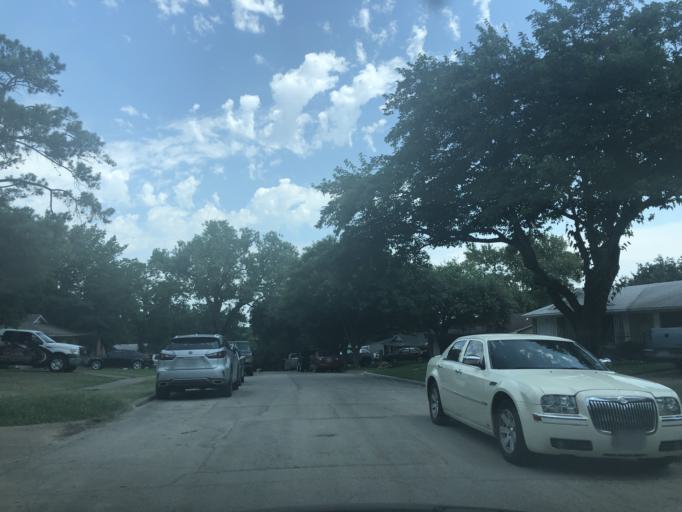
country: US
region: Texas
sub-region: Dallas County
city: Grand Prairie
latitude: 32.7227
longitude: -97.0120
